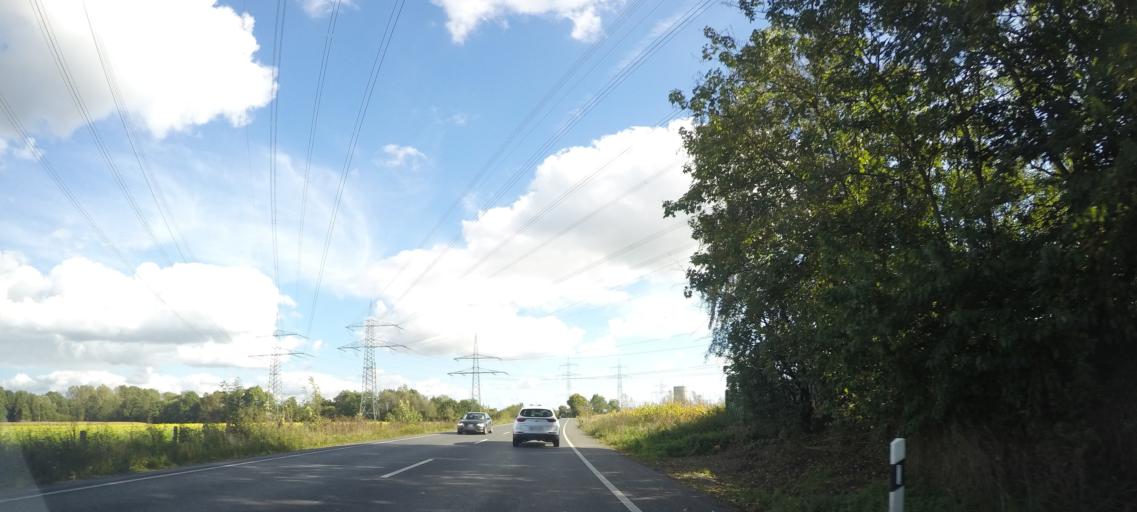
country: DE
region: North Rhine-Westphalia
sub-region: Regierungsbezirk Arnsberg
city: Welver
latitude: 51.6977
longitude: 7.9611
